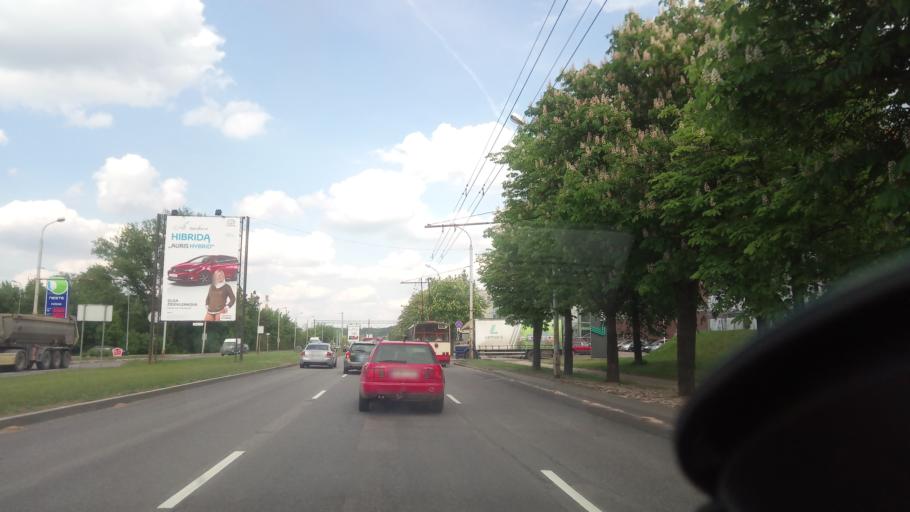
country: LT
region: Vilnius County
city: Lazdynai
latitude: 54.6477
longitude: 25.2102
